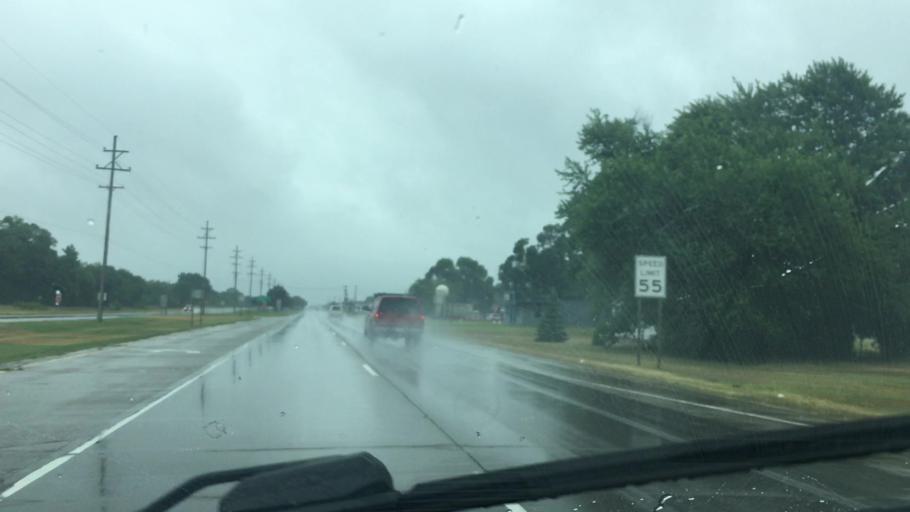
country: US
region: Michigan
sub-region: Ottawa County
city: Jenison
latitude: 42.8965
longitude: -85.8093
